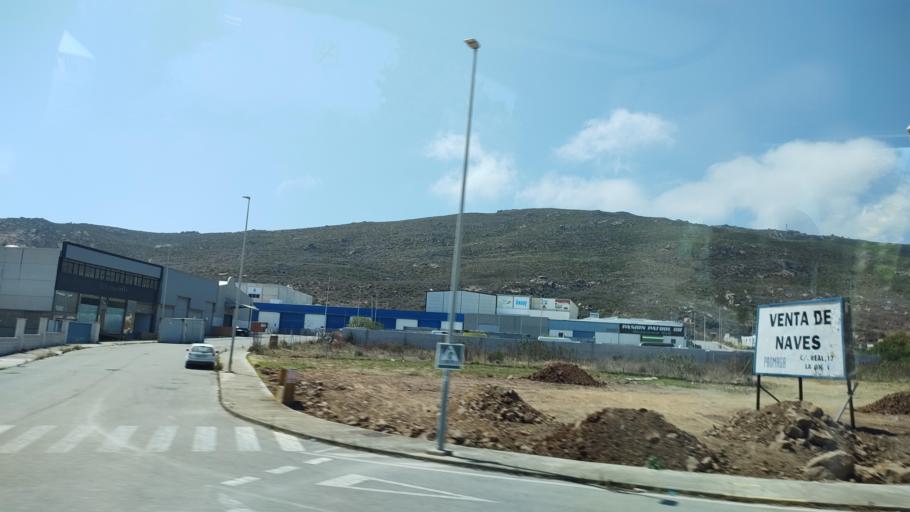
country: ES
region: Andalusia
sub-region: Provincia de Cadiz
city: La Linea de la Concepcion
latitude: 36.1906
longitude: -5.3486
